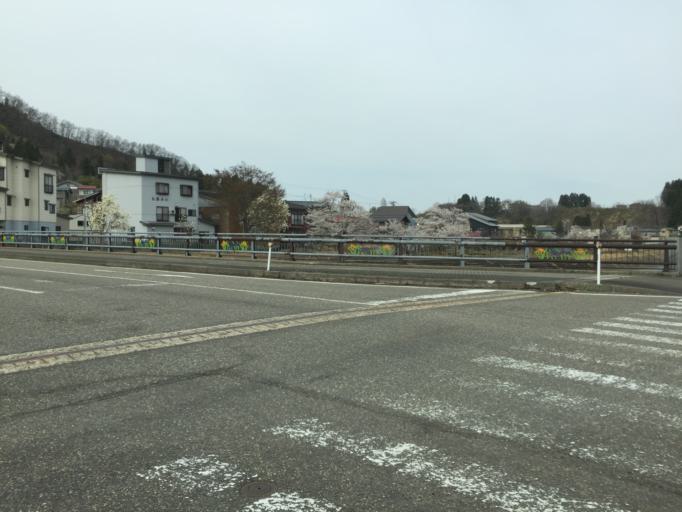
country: JP
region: Niigata
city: Tochio-honcho
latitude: 37.4663
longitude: 138.9893
